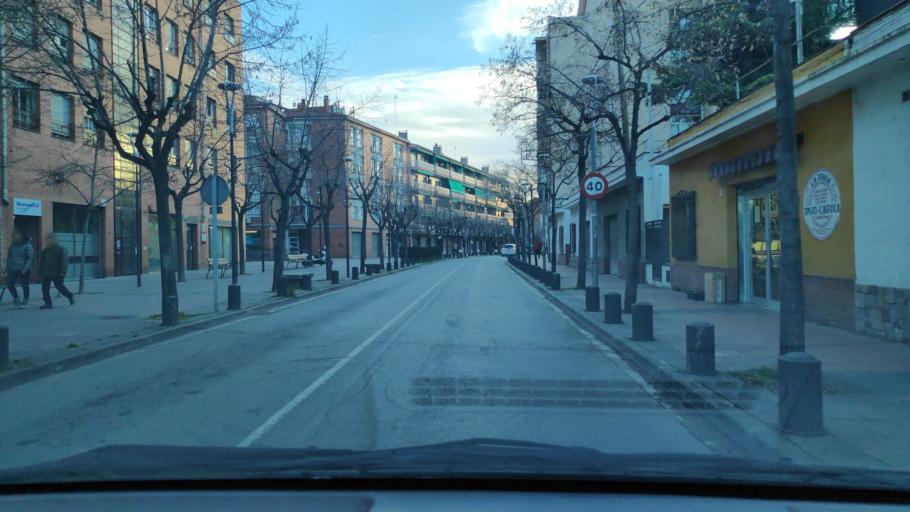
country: ES
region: Catalonia
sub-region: Provincia de Barcelona
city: Montmelo
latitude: 41.5534
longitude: 2.2500
